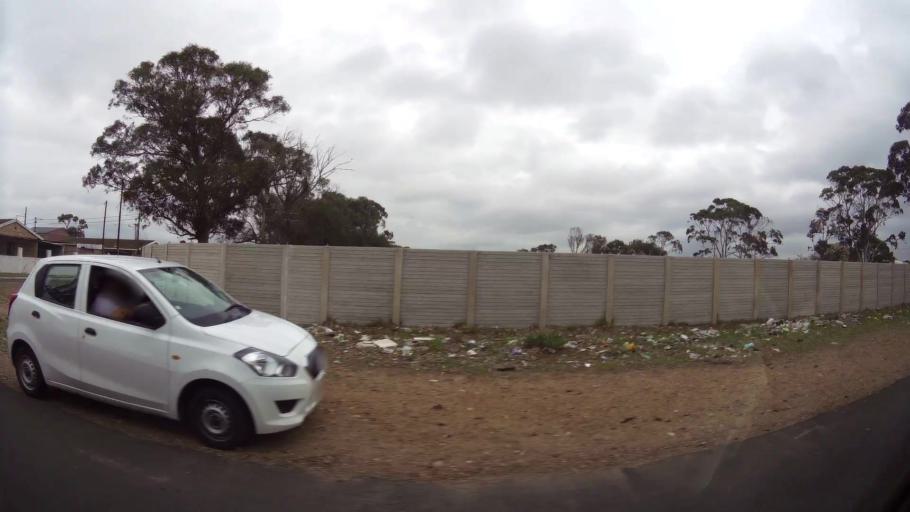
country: ZA
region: Eastern Cape
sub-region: Nelson Mandela Bay Metropolitan Municipality
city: Port Elizabeth
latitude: -33.9021
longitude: 25.5677
